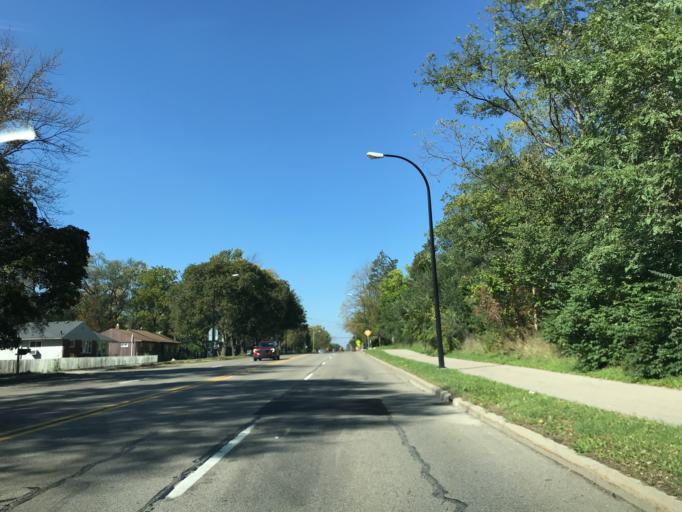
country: US
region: Michigan
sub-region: Washtenaw County
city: Ann Arbor
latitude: 42.2639
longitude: -83.7172
